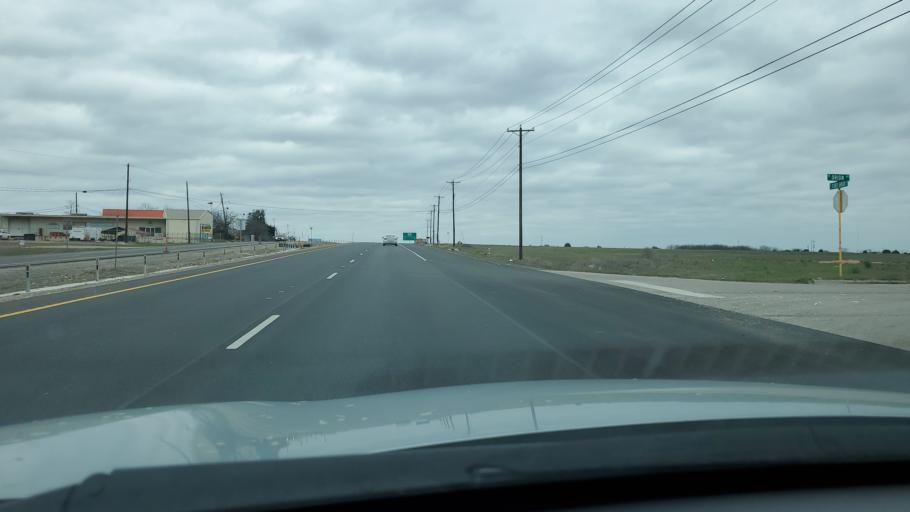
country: US
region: Texas
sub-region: Bell County
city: Killeen
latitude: 31.0715
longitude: -97.7609
